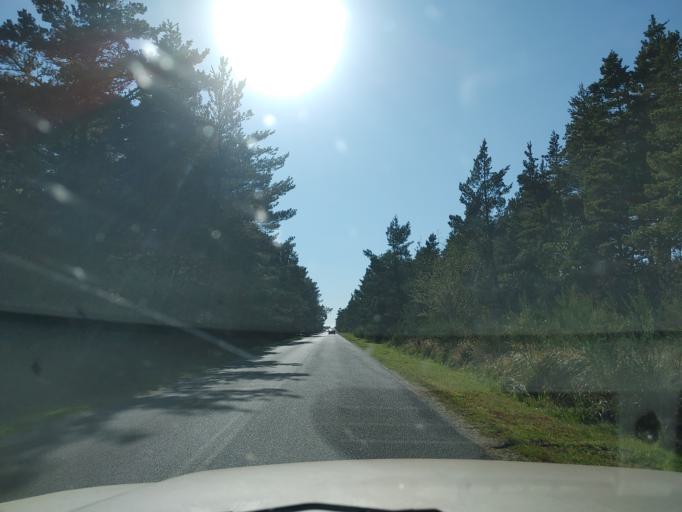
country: US
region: Oregon
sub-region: Clatsop County
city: Warrenton
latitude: 46.1793
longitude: -123.9736
